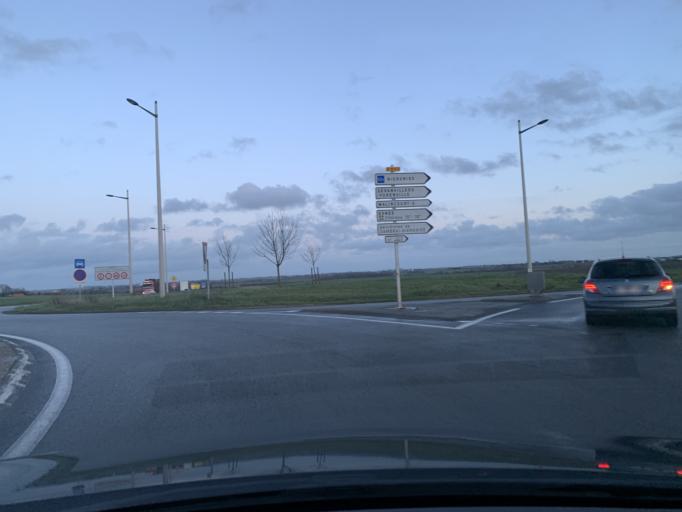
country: FR
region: Nord-Pas-de-Calais
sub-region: Departement du Nord
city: Cambrai
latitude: 50.1518
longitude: 3.2639
